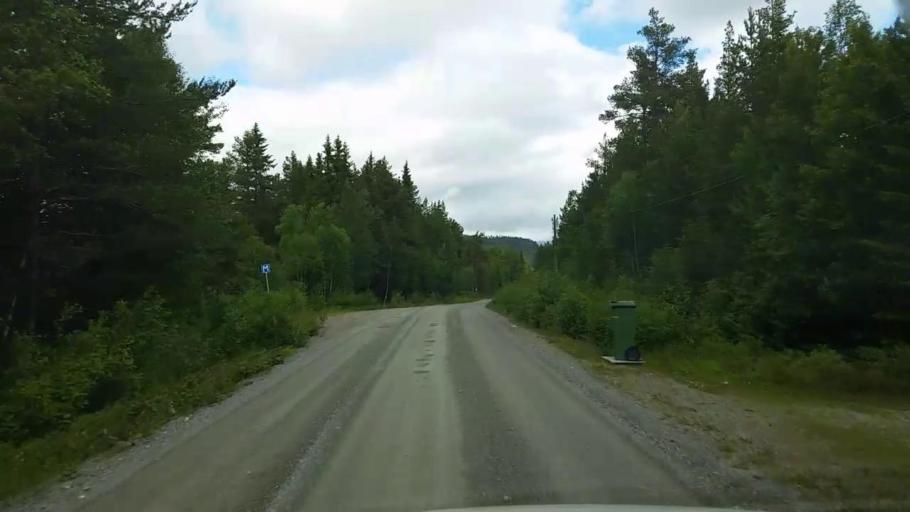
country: NO
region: Hedmark
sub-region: Engerdal
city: Engerdal
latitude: 62.4234
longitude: 12.6765
